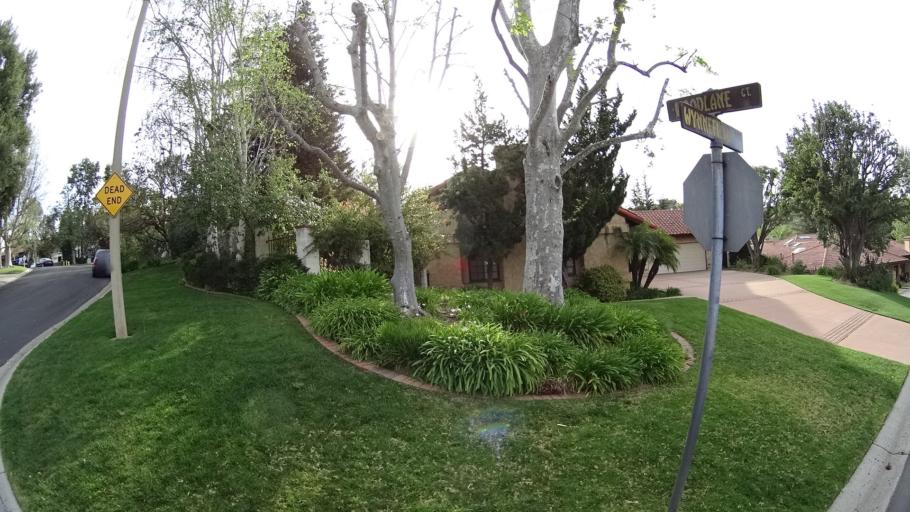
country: US
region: California
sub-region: Ventura County
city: Thousand Oaks
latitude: 34.1930
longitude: -118.8188
